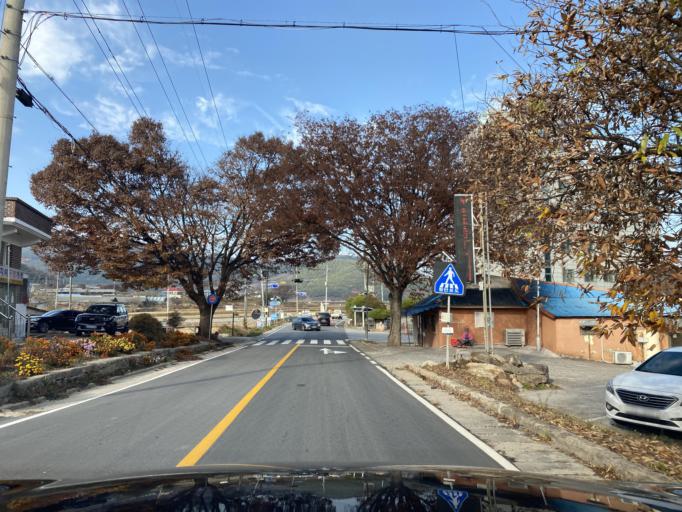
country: KR
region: Chungcheongnam-do
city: Hongsung
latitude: 36.6742
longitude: 126.6425
